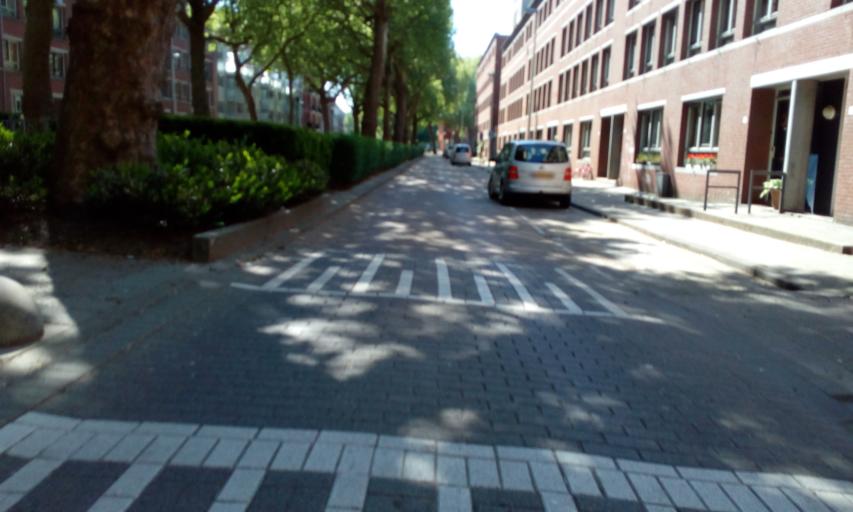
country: NL
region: South Holland
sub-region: Gemeente Rotterdam
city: Rotterdam
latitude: 51.9372
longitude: 4.4932
